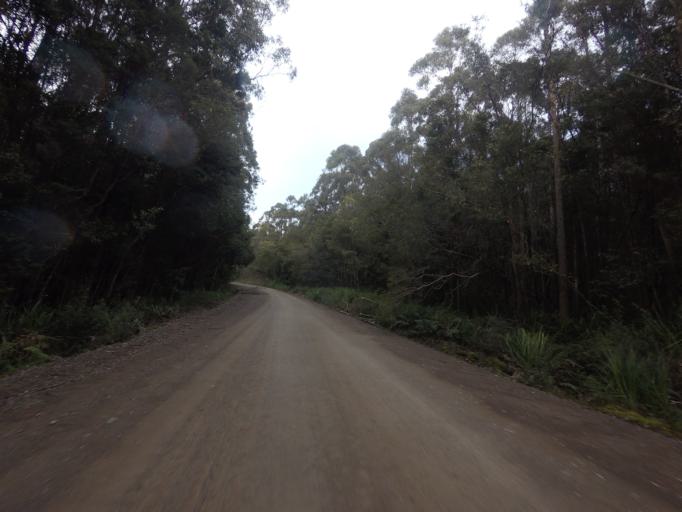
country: AU
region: Tasmania
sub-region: Huon Valley
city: Geeveston
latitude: -43.5208
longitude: 146.8826
